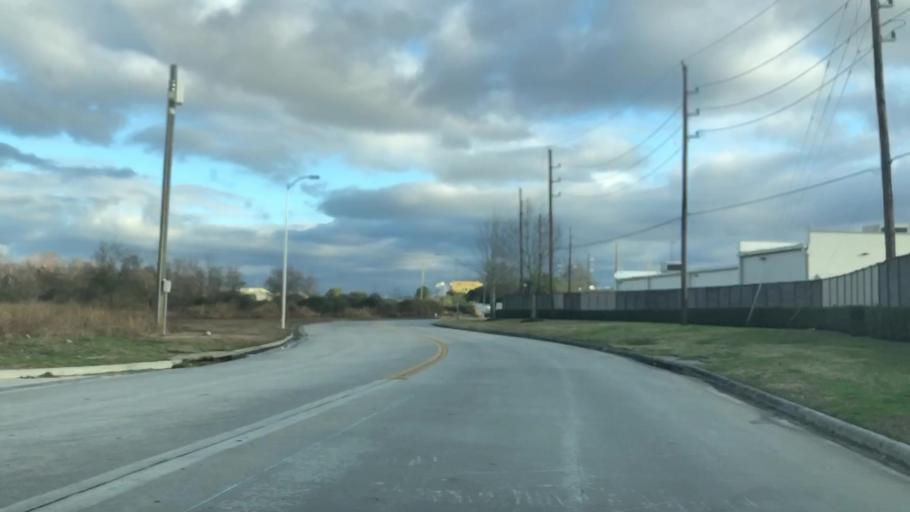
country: US
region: Texas
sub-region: Harris County
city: Aldine
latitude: 29.9179
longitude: -95.4167
